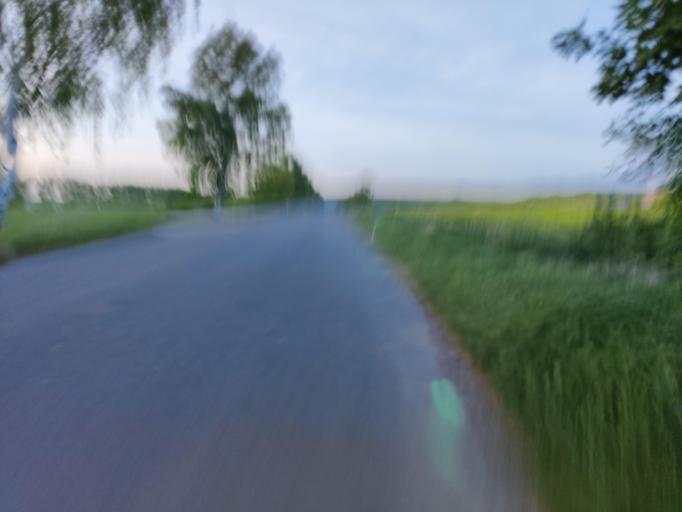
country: DE
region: Saxony-Anhalt
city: Karsdorf
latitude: 51.2655
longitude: 11.6475
